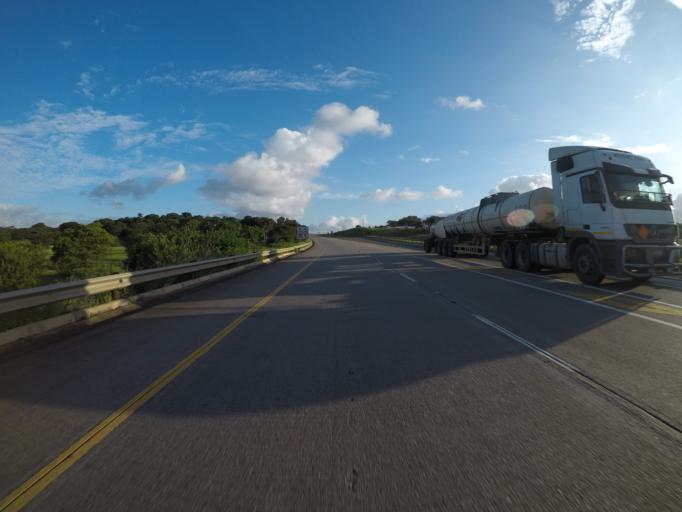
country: ZA
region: KwaZulu-Natal
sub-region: uMkhanyakude District Municipality
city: Mtubatuba
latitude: -28.5037
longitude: 32.1375
